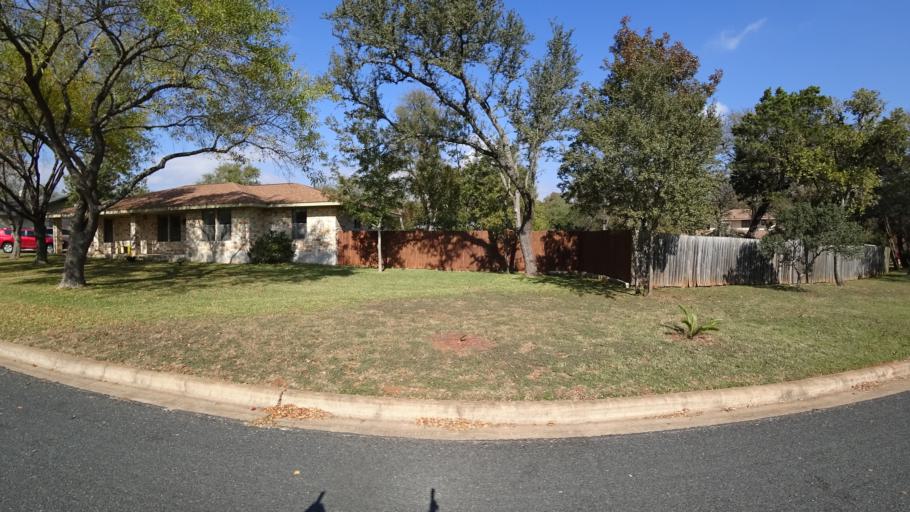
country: US
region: Texas
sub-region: Travis County
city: Shady Hollow
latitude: 30.1652
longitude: -97.8635
